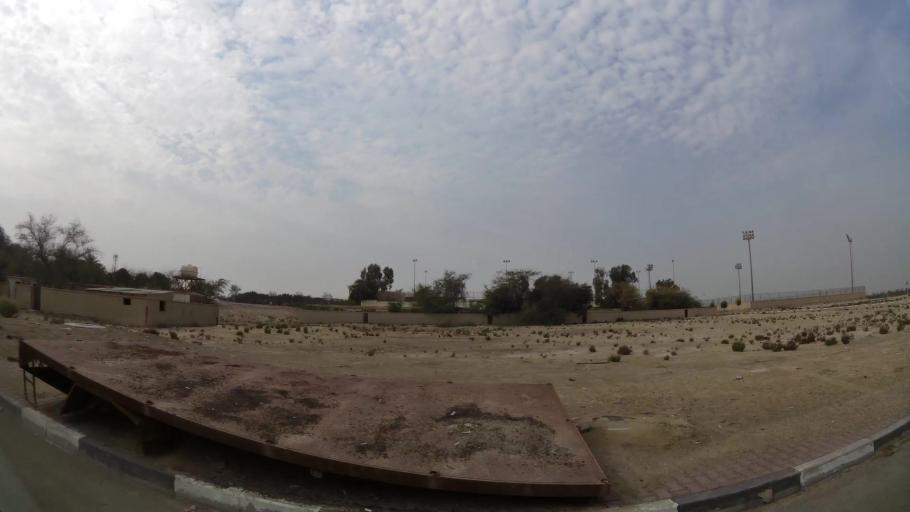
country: AE
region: Abu Dhabi
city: Abu Dhabi
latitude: 24.6875
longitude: 54.7671
